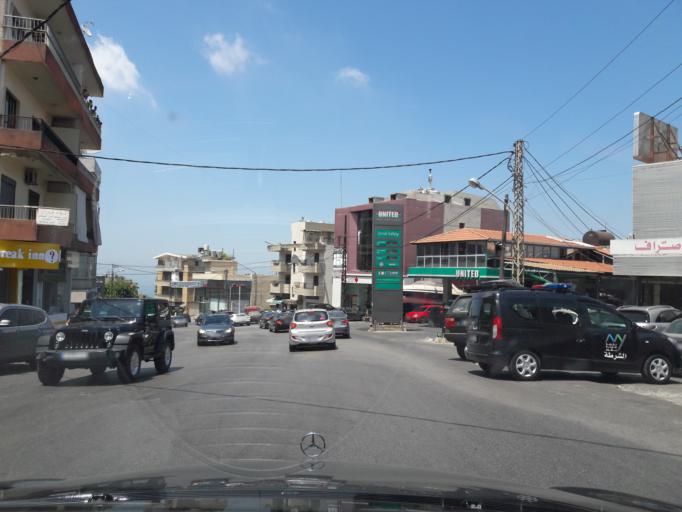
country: LB
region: Mont-Liban
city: Djounie
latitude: 33.9255
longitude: 35.6327
